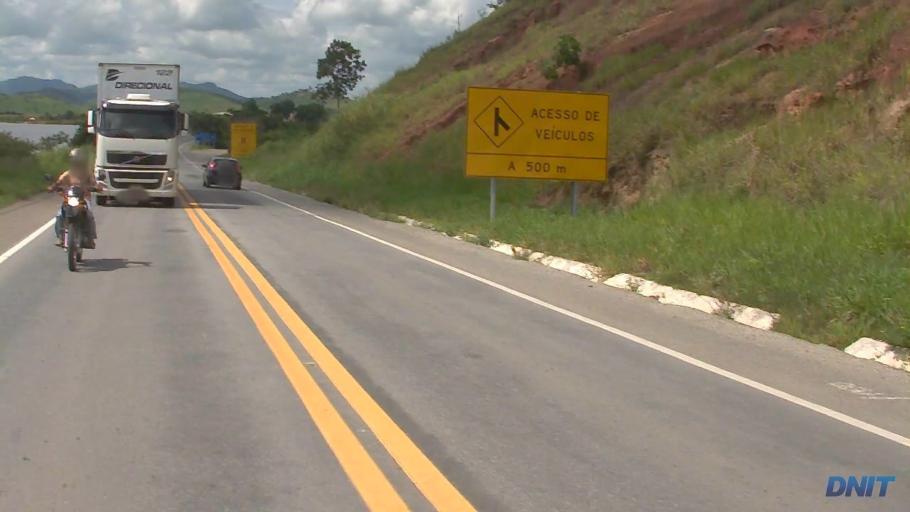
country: BR
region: Minas Gerais
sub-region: Governador Valadares
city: Governador Valadares
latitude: -19.0450
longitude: -42.1525
